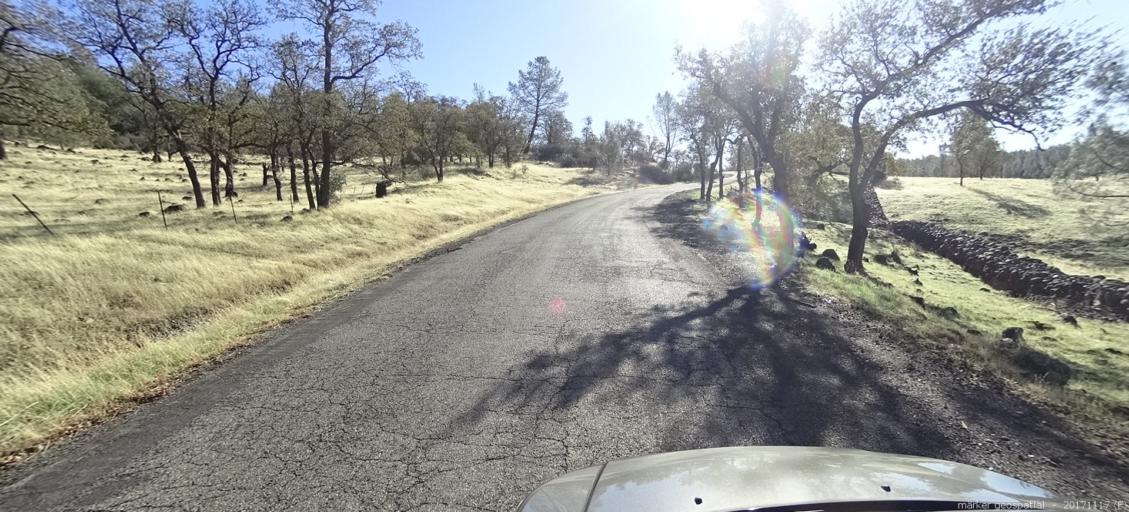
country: US
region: California
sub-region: Shasta County
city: Cottonwood
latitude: 40.4391
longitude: -122.1235
